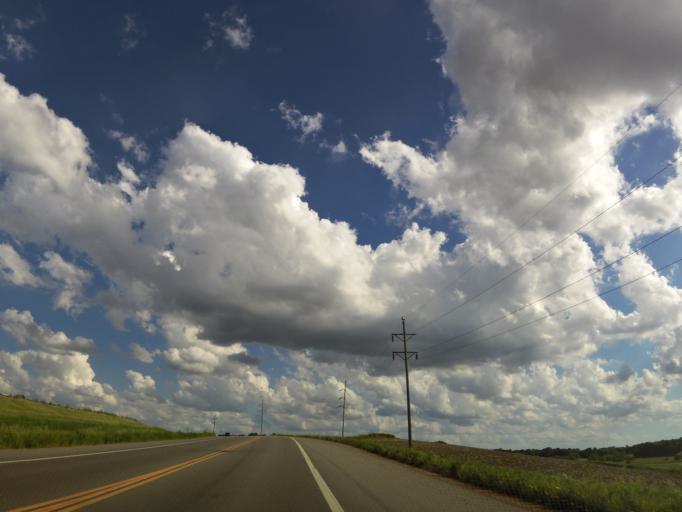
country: US
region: Minnesota
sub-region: Carver County
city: Waconia
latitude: 44.8895
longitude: -93.8185
